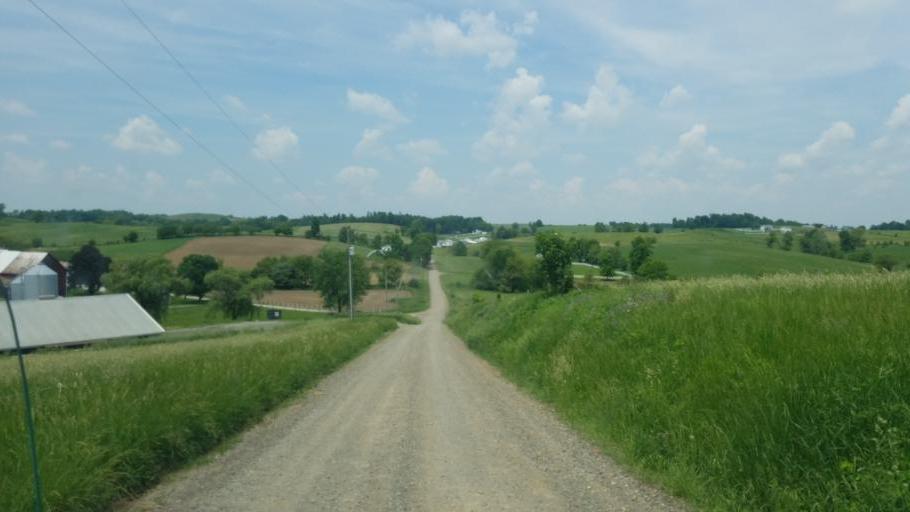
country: US
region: Ohio
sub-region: Tuscarawas County
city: Sugarcreek
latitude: 40.4705
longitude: -81.7563
